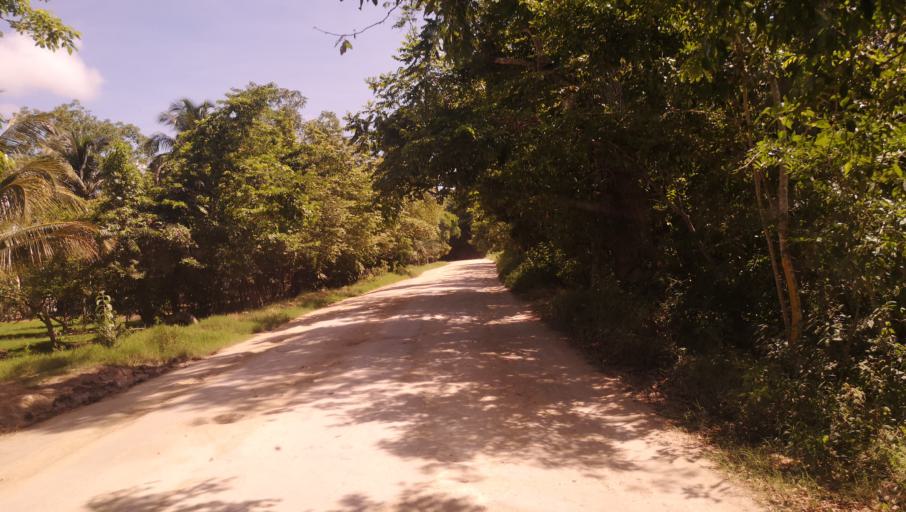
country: GT
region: Peten
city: Melchor de Mencos
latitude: 16.9775
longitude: -89.2631
